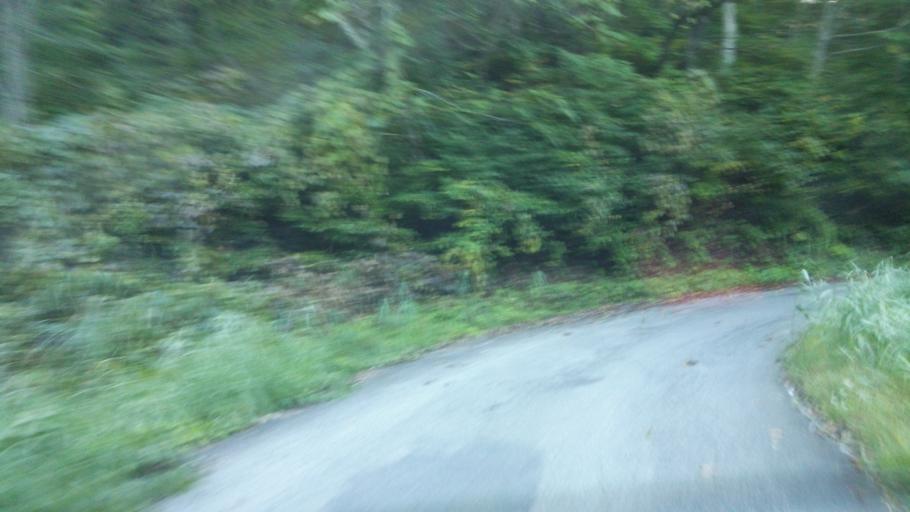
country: JP
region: Fukushima
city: Kitakata
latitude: 37.4706
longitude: 139.7312
